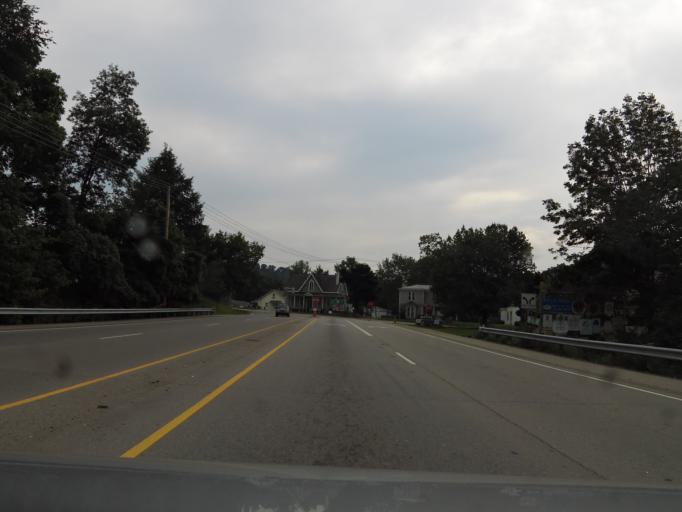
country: US
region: Ohio
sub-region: Brown County
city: Ripley
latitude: 38.7419
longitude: -83.8420
